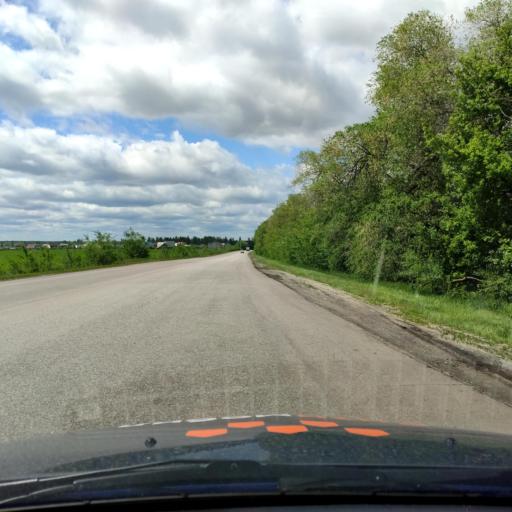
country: RU
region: Voronezj
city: Novaya Usman'
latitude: 51.5891
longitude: 39.3356
